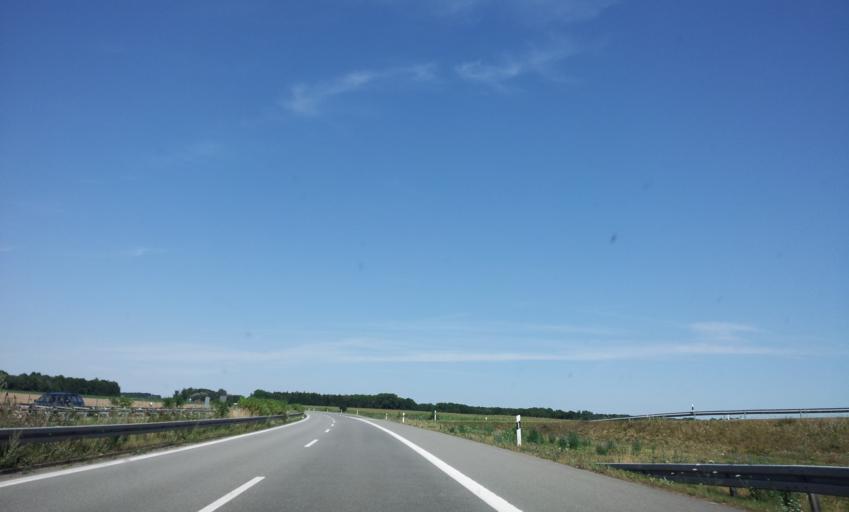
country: DE
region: Mecklenburg-Vorpommern
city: Jarmen
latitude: 53.9482
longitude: 13.3680
